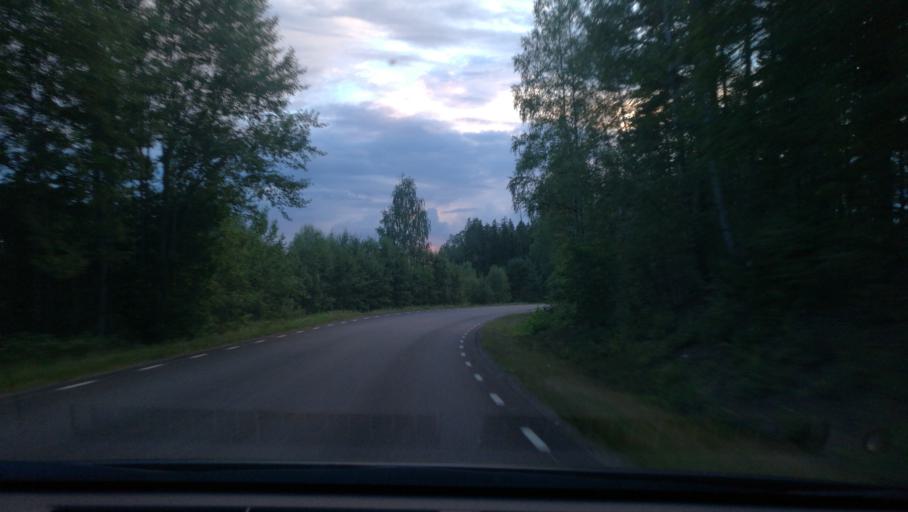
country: SE
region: OEstergoetland
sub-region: Norrkopings Kommun
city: Svartinge
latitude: 58.8194
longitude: 16.0047
